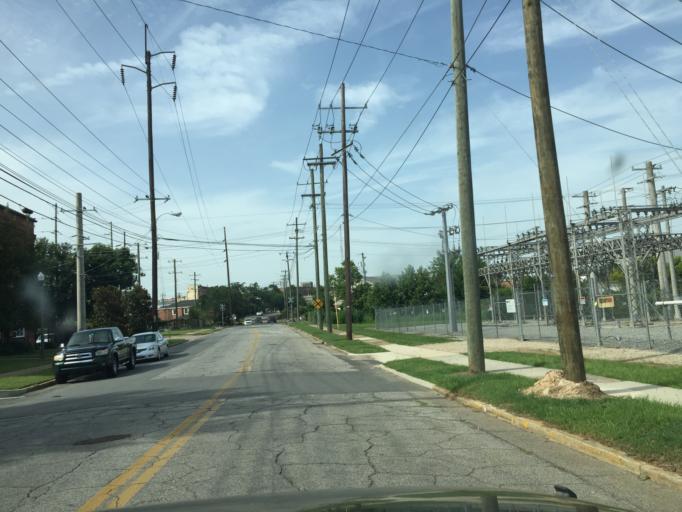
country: US
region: Georgia
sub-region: Thomas County
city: Thomasville
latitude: 30.8335
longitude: -83.9814
